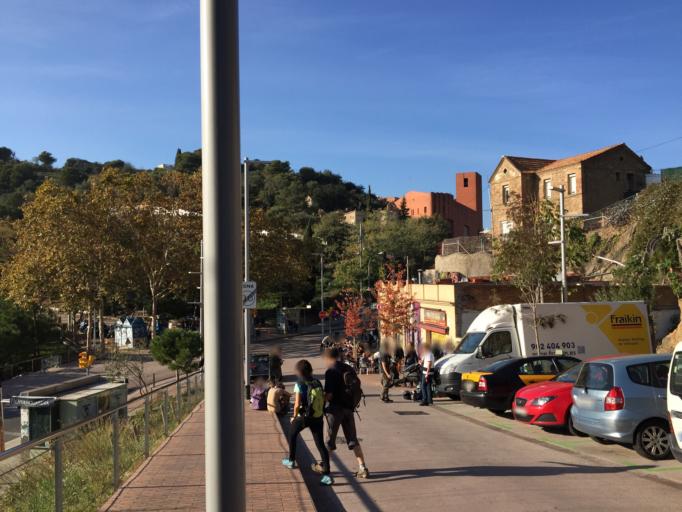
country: ES
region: Catalonia
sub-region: Provincia de Barcelona
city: Horta-Guinardo
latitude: 41.4180
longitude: 2.1580
